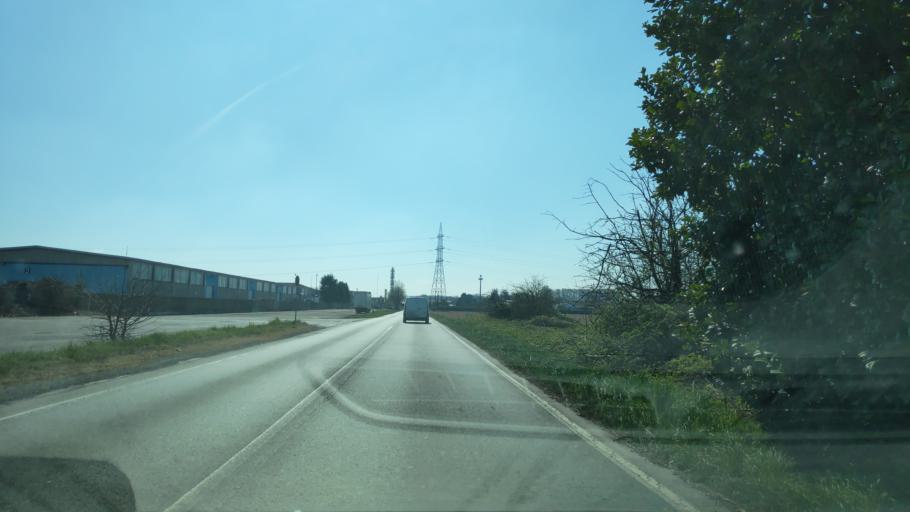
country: IT
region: Lombardy
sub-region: Citta metropolitana di Milano
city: Settala
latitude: 45.4583
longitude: 9.3803
